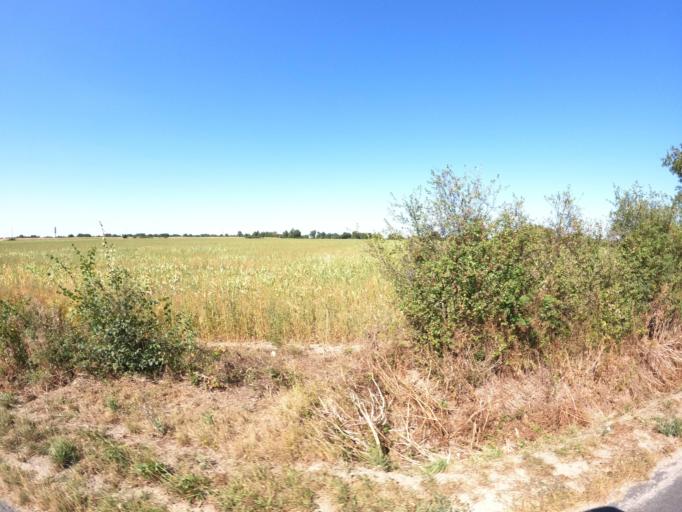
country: FR
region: Pays de la Loire
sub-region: Departement de la Vendee
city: La Boissiere-de-Montaigu
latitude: 46.9541
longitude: -1.2206
